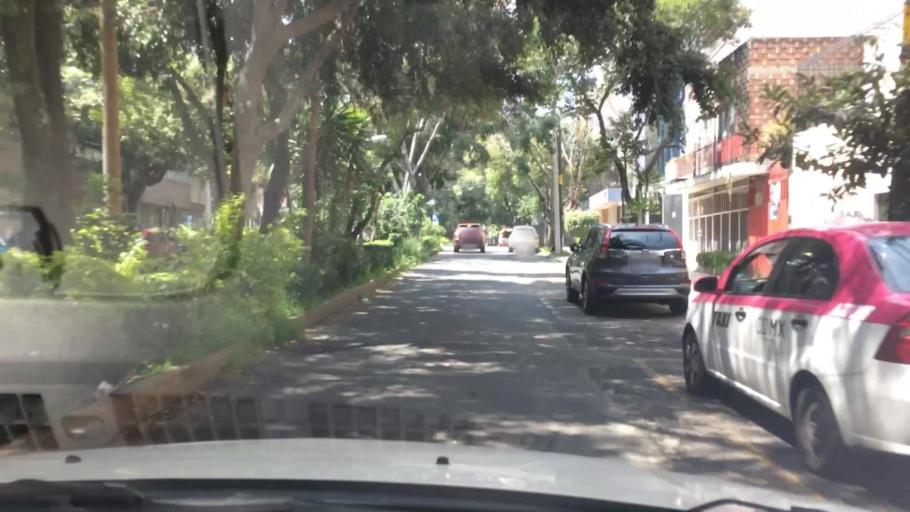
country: MX
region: Mexico City
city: Alvaro Obregon
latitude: 19.3647
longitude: -99.1831
